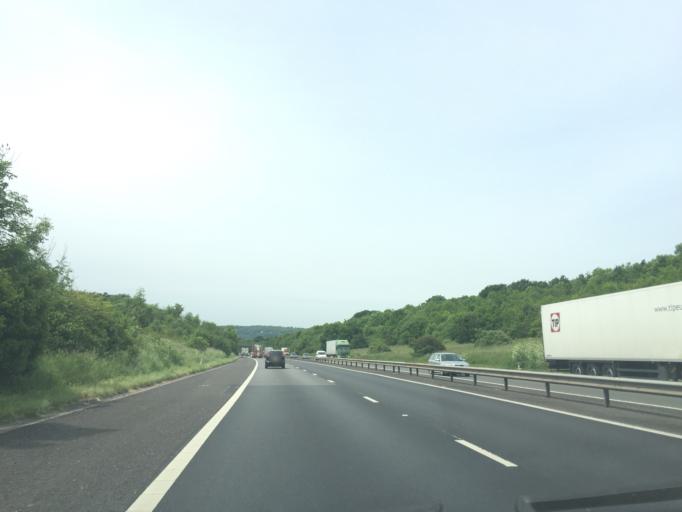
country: GB
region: England
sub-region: Kent
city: Kemsing
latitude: 51.3024
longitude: 0.2121
